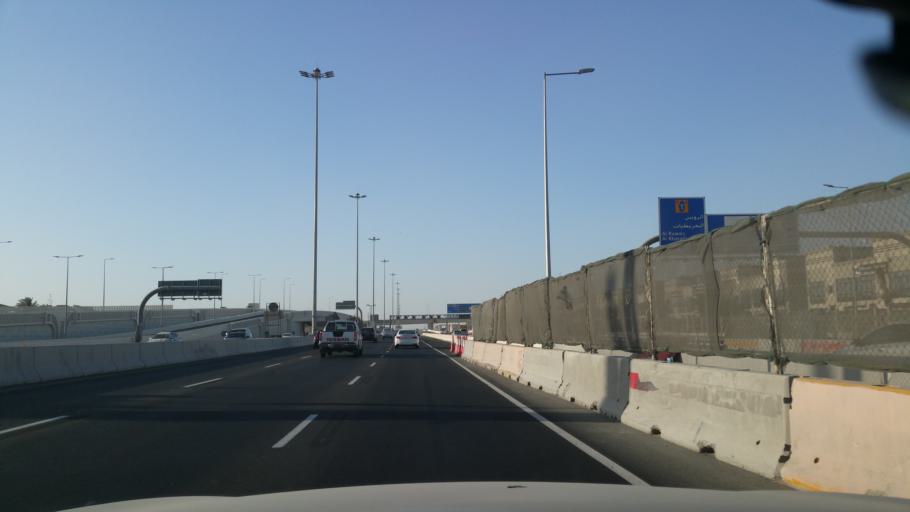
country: QA
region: Baladiyat ar Rayyan
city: Ar Rayyan
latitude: 25.3386
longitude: 51.4612
